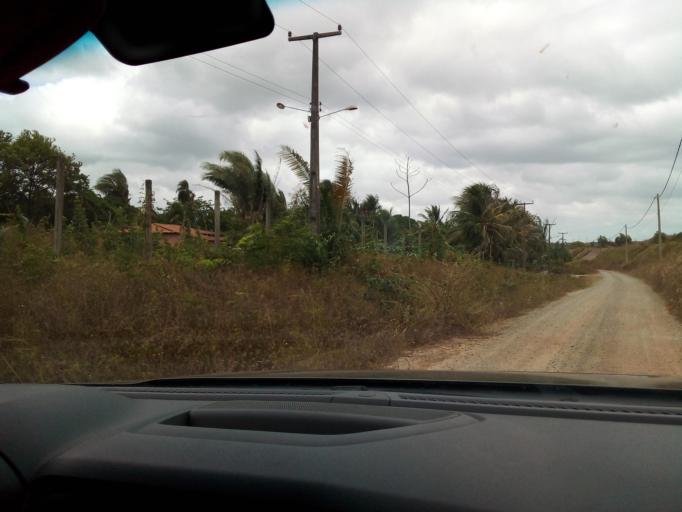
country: BR
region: Maranhao
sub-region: Sao Luis
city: Sao Luis
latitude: -2.6705
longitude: -44.2944
